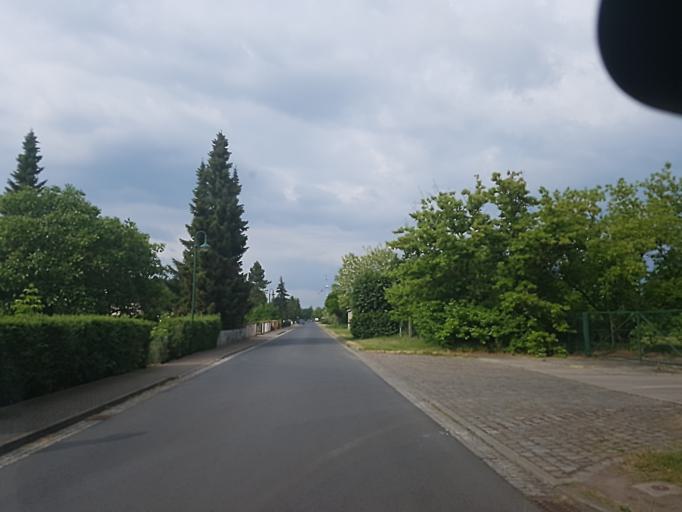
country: DE
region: Saxony-Anhalt
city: Muhlanger
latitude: 51.8551
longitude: 12.7280
